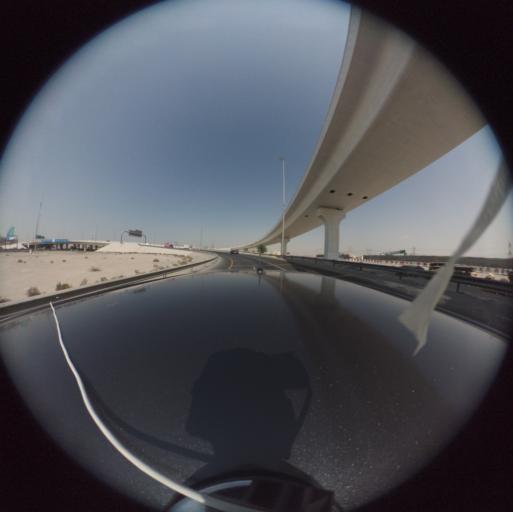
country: AE
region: Dubai
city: Dubai
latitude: 25.1435
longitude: 55.2616
